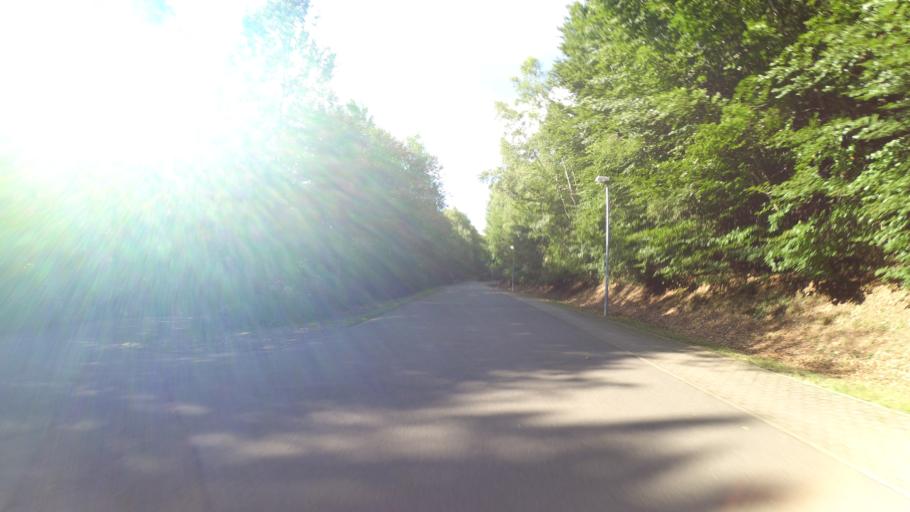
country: DE
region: Saarland
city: Nonnweiler
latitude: 49.6089
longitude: 6.9752
